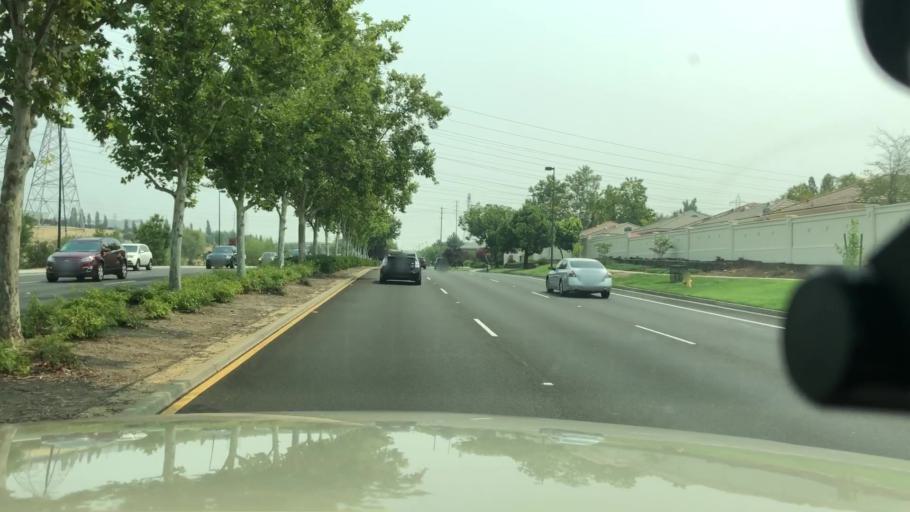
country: US
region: California
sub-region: Sacramento County
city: Folsom
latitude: 38.6629
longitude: -121.1352
